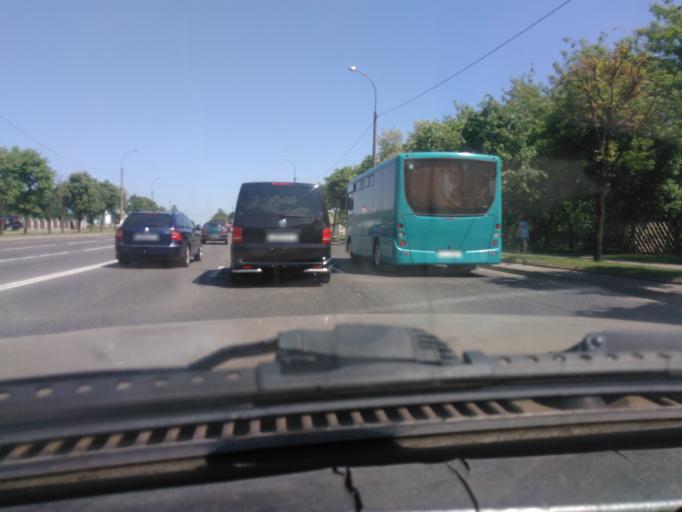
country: BY
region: Mogilev
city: Mahilyow
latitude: 53.9090
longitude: 30.3583
